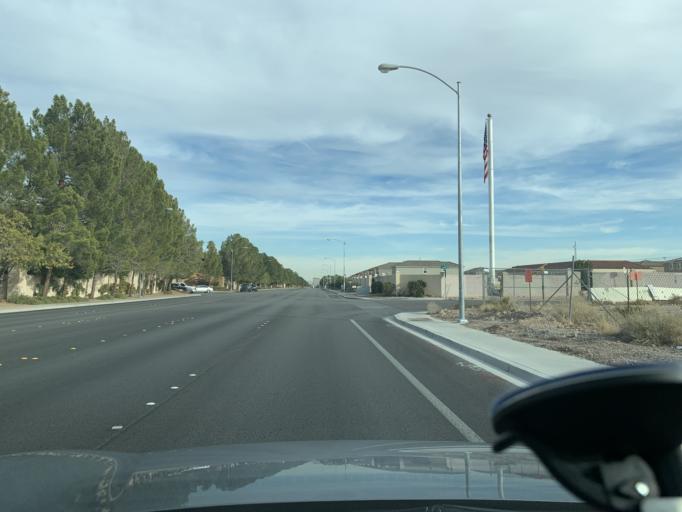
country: US
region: Nevada
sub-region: Clark County
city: Spring Valley
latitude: 36.0923
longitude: -115.2525
